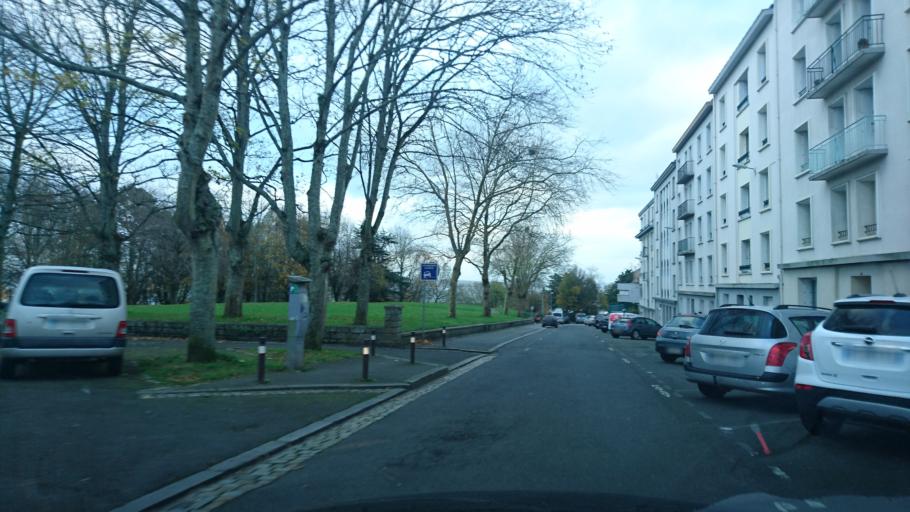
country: FR
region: Brittany
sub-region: Departement du Finistere
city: Brest
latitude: 48.3866
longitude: -4.4843
